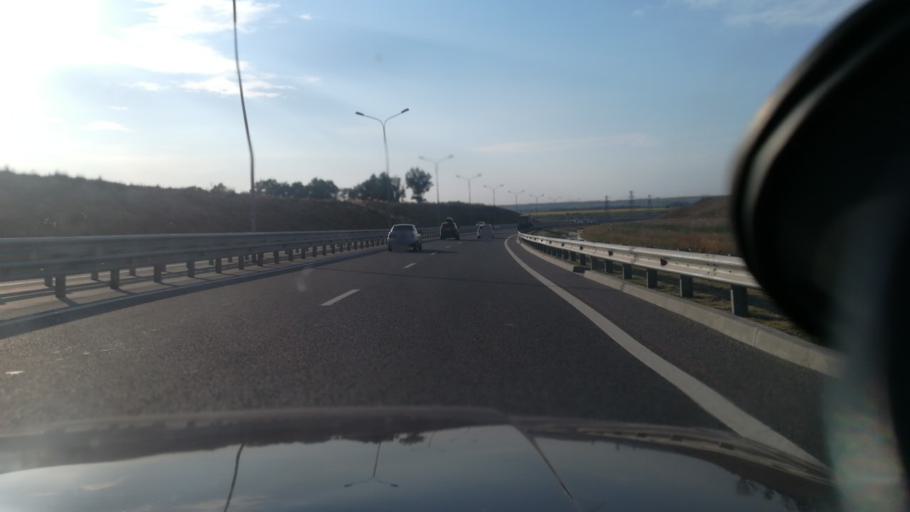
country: RU
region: Krasnodarskiy
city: Dzhiginka
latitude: 45.1226
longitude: 37.3133
